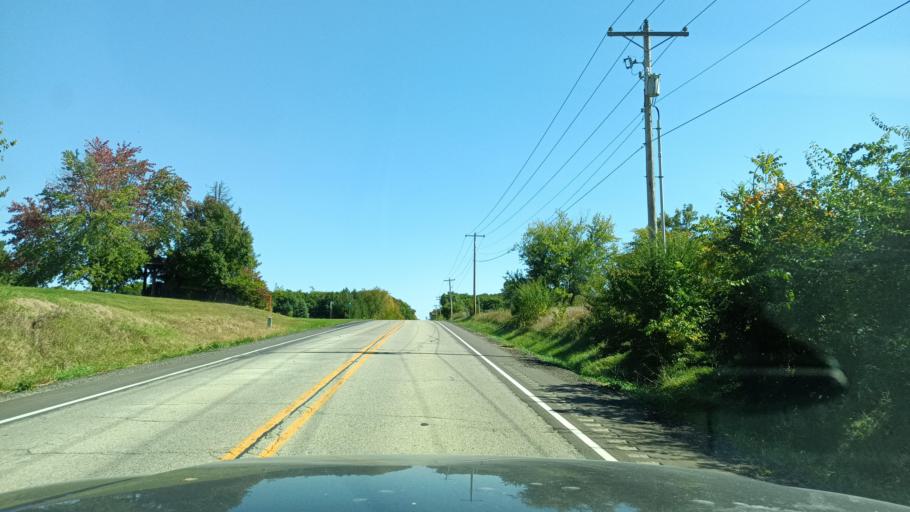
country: US
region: Illinois
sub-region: McLean County
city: Danvers
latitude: 40.6170
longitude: -89.2216
